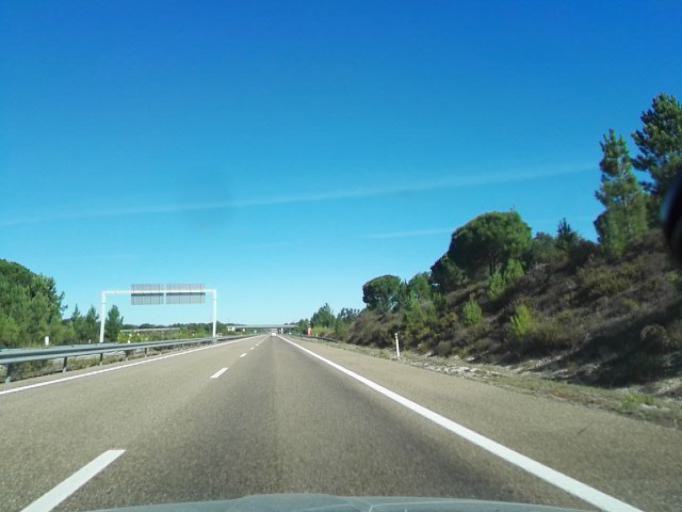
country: PT
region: Evora
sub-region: Vendas Novas
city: Vendas Novas
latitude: 38.6160
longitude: -8.6520
